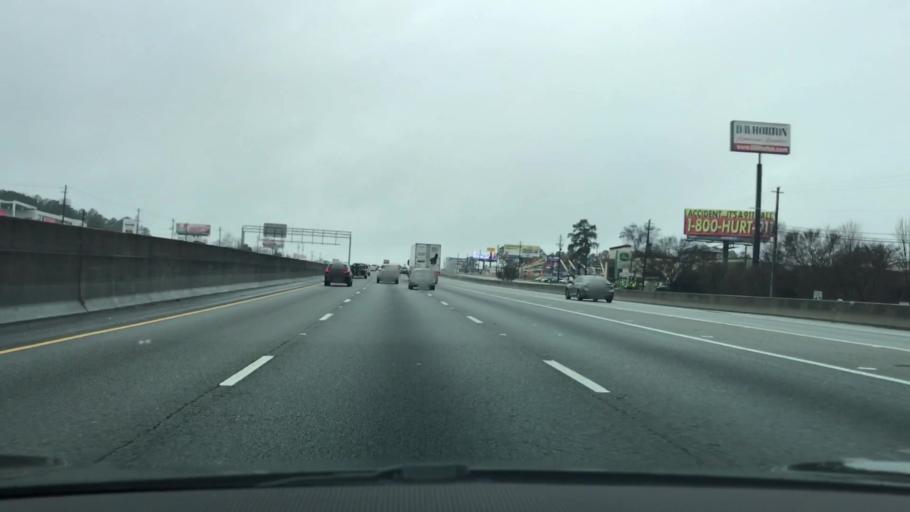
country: US
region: Georgia
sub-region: Rockdale County
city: Conyers
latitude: 33.6661
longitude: -84.0320
